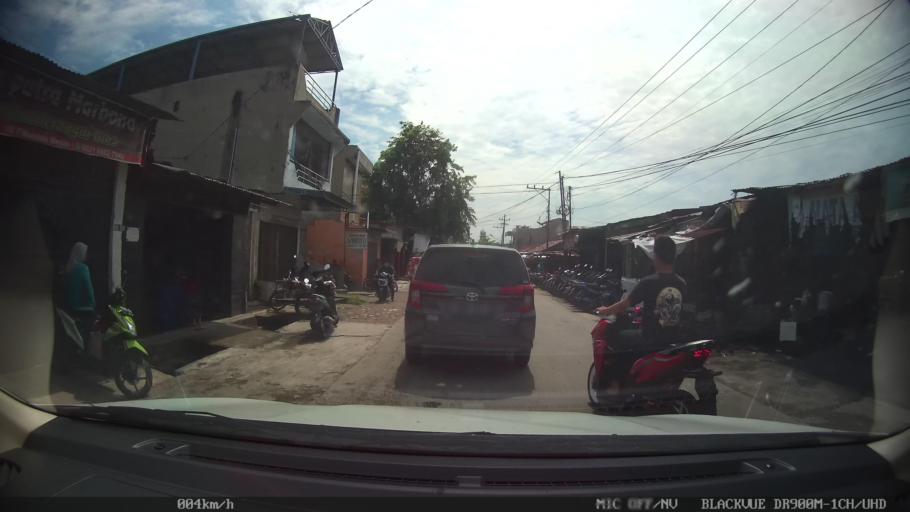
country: ID
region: North Sumatra
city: Medan
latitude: 3.5873
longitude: 98.7181
